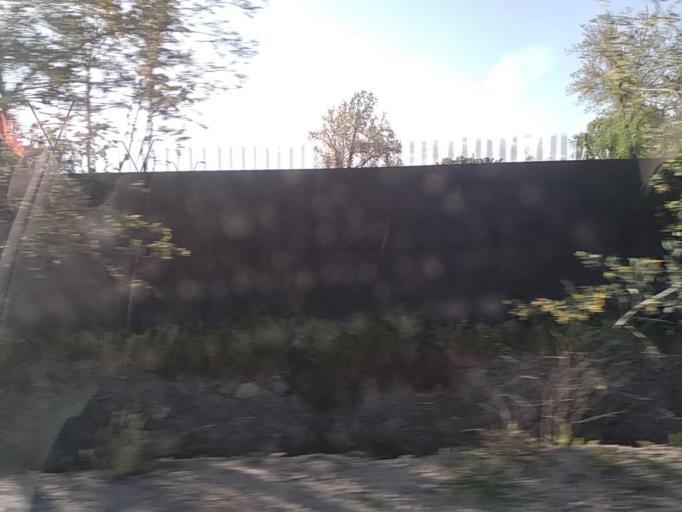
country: CL
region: Santiago Metropolitan
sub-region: Provincia de Chacabuco
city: Chicureo Abajo
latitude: -33.3128
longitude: -70.7218
